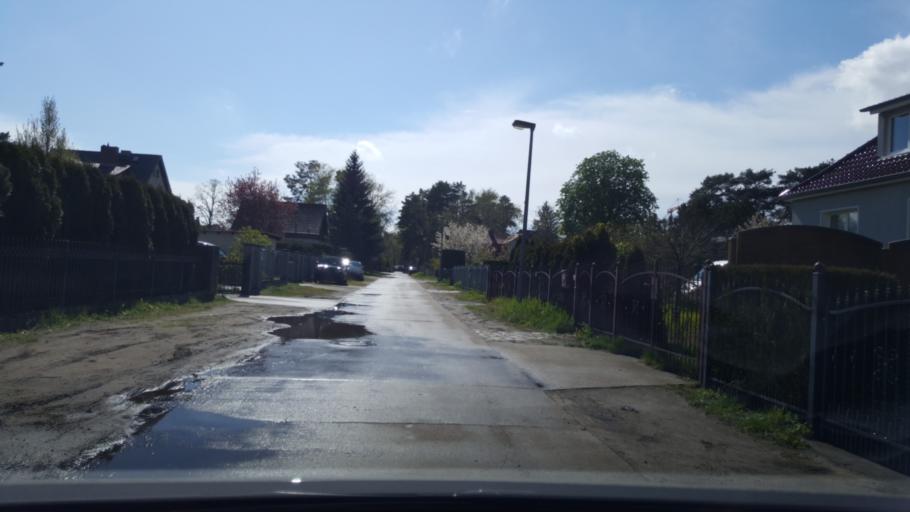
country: DE
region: Berlin
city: Bohnsdorf
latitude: 52.3955
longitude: 13.5872
